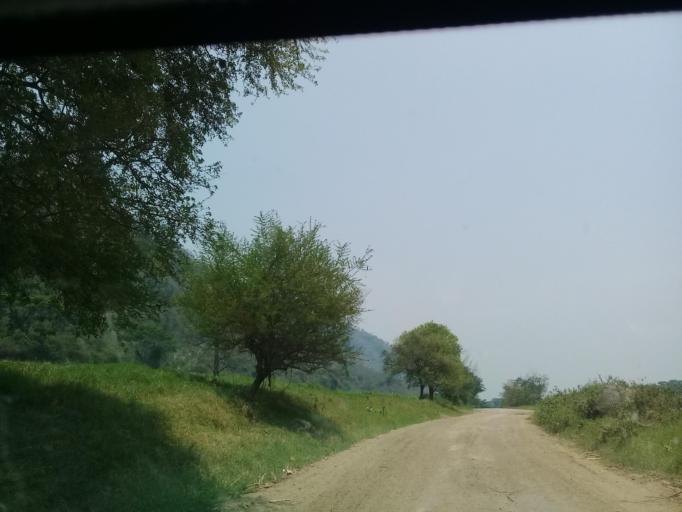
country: MX
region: Veracruz
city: Tezonapa
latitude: 18.6199
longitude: -96.6976
